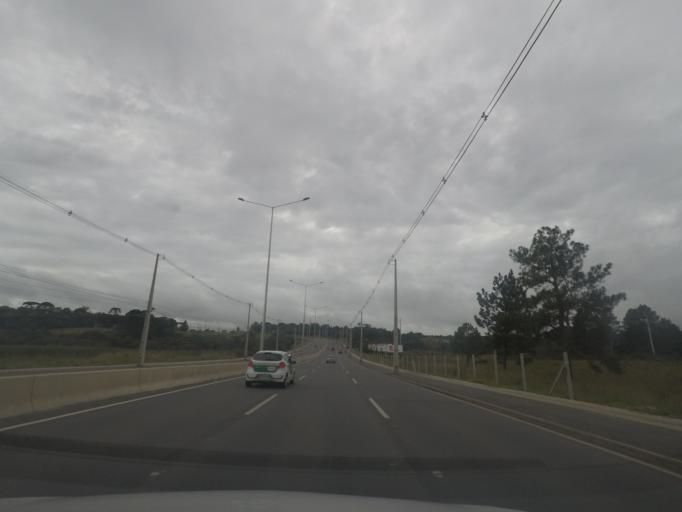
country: BR
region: Parana
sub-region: Piraquara
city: Piraquara
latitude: -25.4606
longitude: -49.0846
